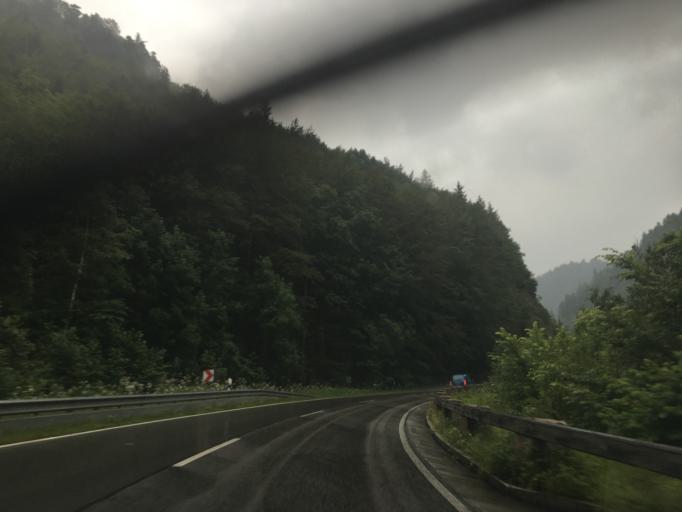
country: DE
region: Bavaria
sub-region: Upper Bavaria
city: Reit im Winkl
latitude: 47.6977
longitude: 12.4836
